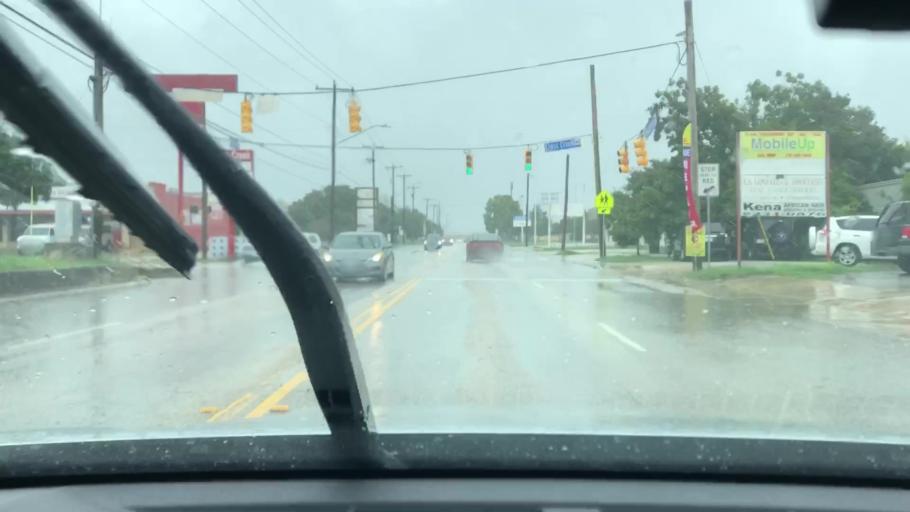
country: US
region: Texas
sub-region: Bexar County
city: Windcrest
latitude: 29.5103
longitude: -98.4033
